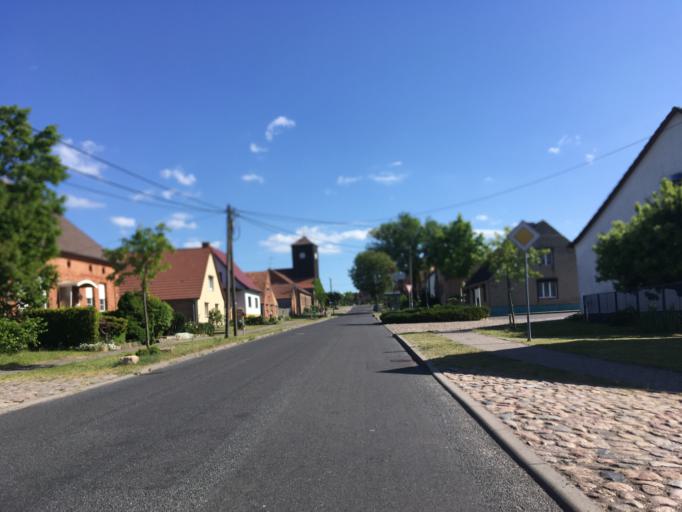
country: DE
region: Brandenburg
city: Althuttendorf
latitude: 52.9641
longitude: 13.8064
